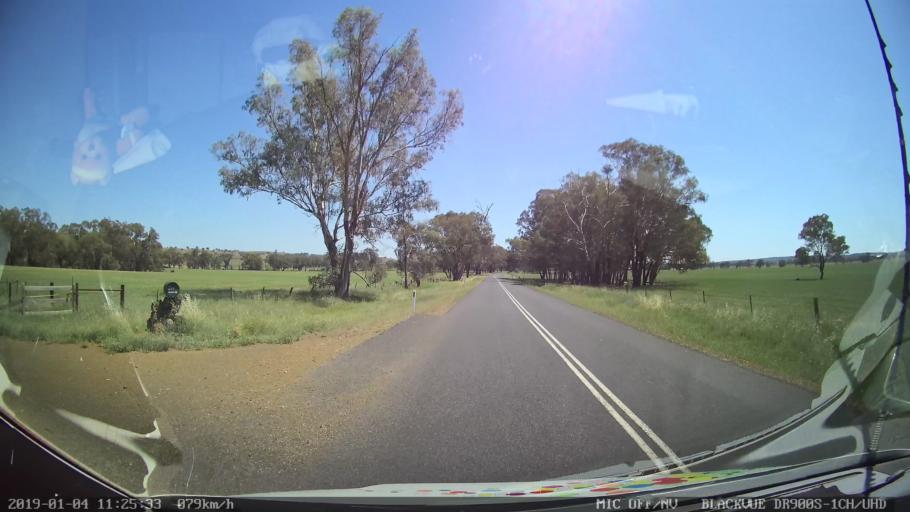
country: AU
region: New South Wales
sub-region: Cabonne
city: Molong
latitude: -33.1235
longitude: 148.7523
